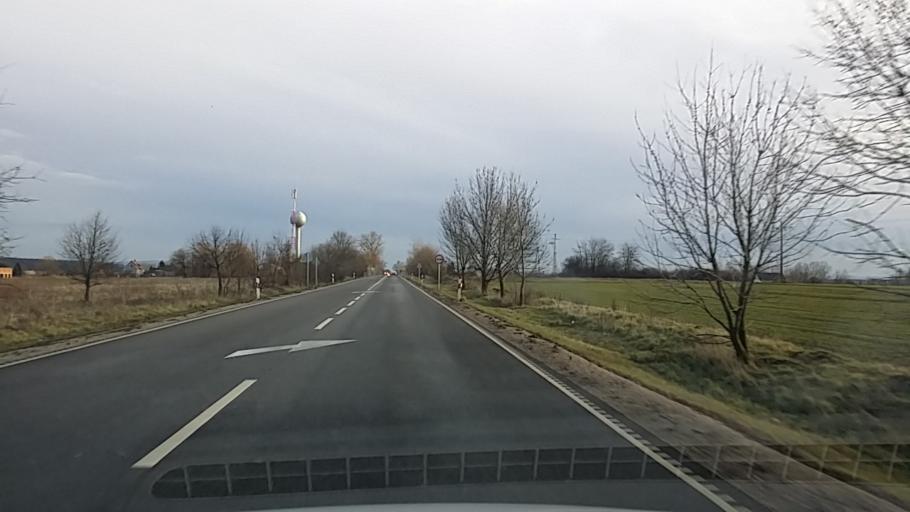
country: HU
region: Komarom-Esztergom
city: Csaszar
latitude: 47.4559
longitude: 18.0972
